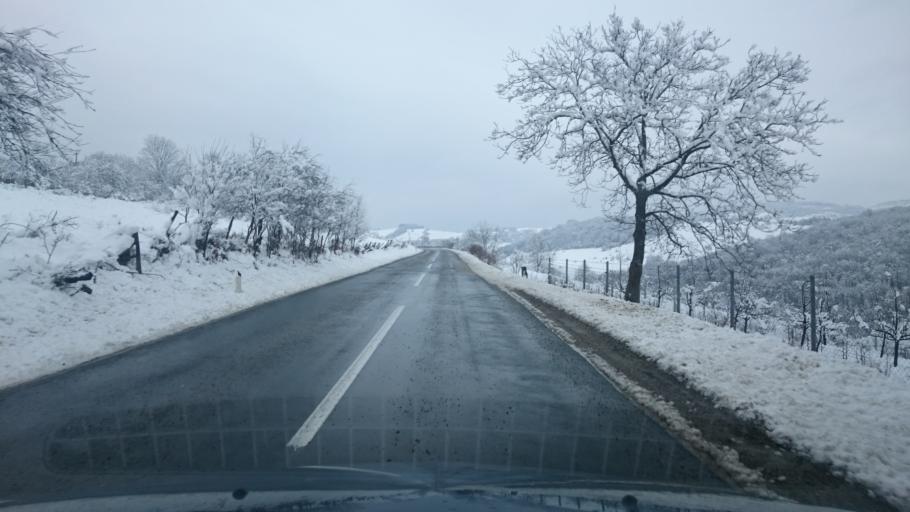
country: BA
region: Republika Srpska
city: Kotor-Varos
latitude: 44.6119
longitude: 17.2361
